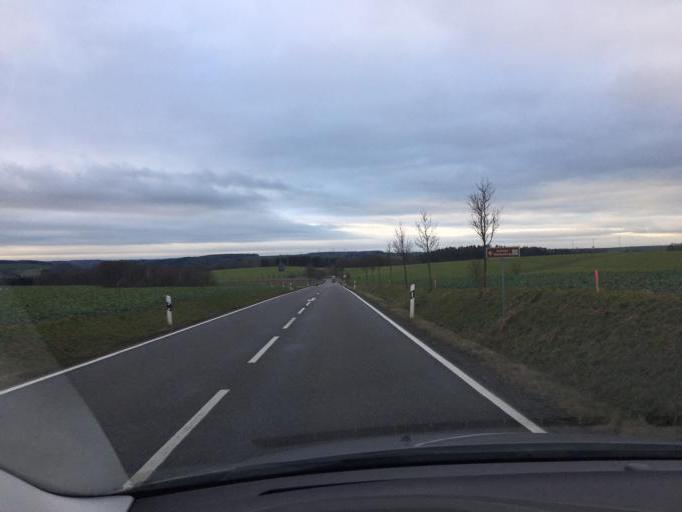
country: DE
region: Thuringia
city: Juckelberg
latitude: 50.9131
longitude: 12.6555
